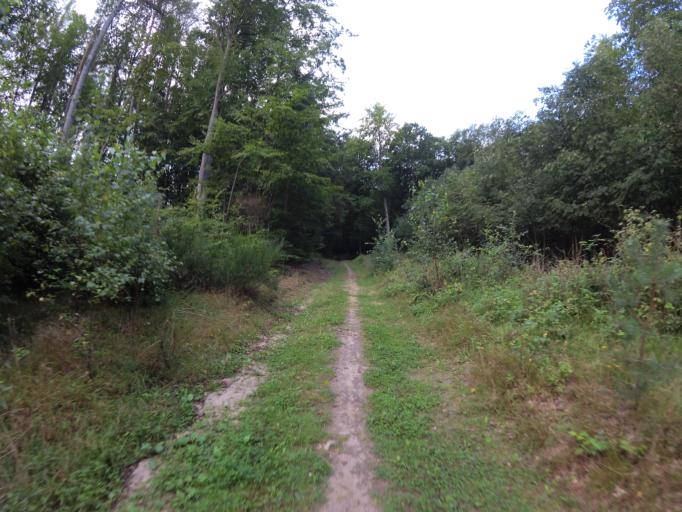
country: PL
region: Pomeranian Voivodeship
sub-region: Gdynia
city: Wielki Kack
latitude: 54.5046
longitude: 18.4382
